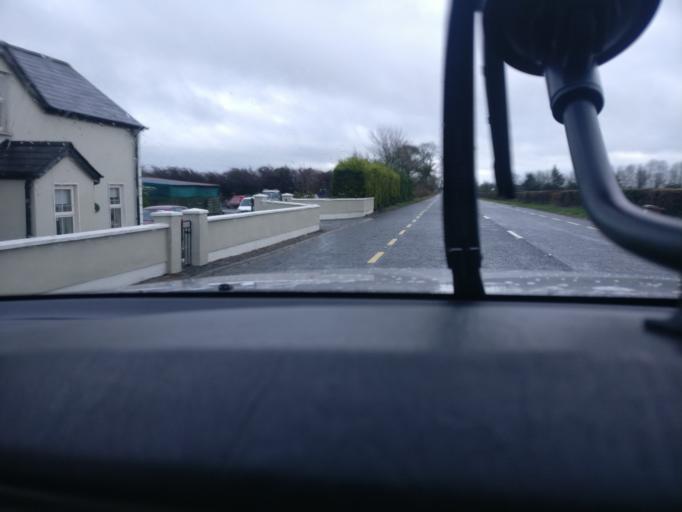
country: IE
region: Leinster
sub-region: An Mhi
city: Enfield
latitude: 53.4208
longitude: -6.8555
